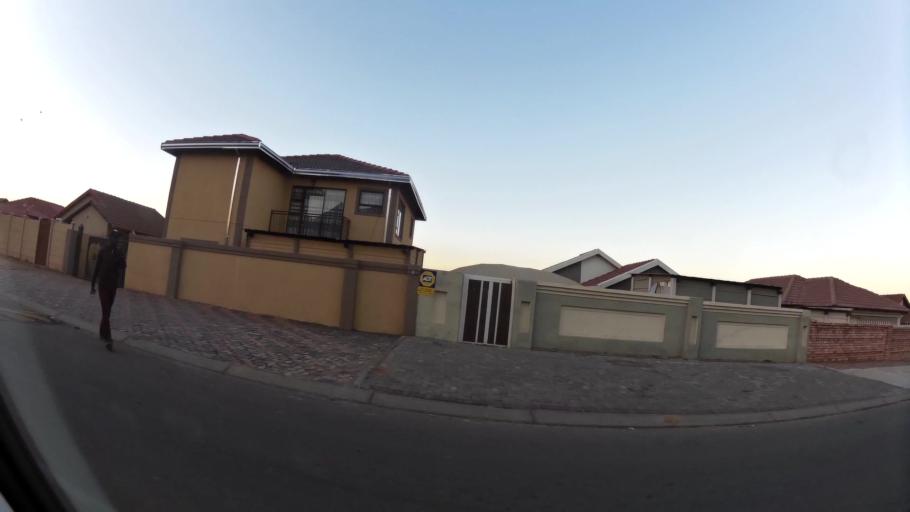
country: ZA
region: North-West
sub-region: Bojanala Platinum District Municipality
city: Rustenburg
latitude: -25.6522
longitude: 27.2069
